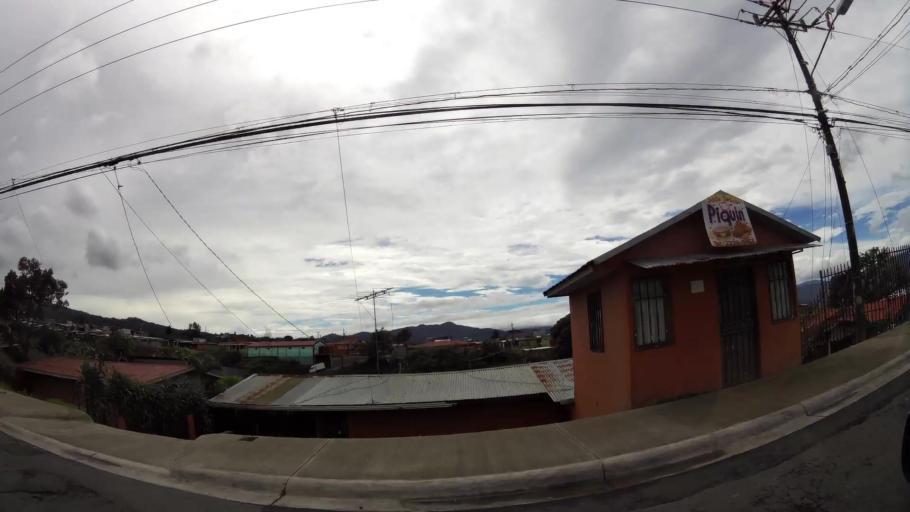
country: CR
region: San Jose
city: Ipis
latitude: 9.9602
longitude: -84.0098
